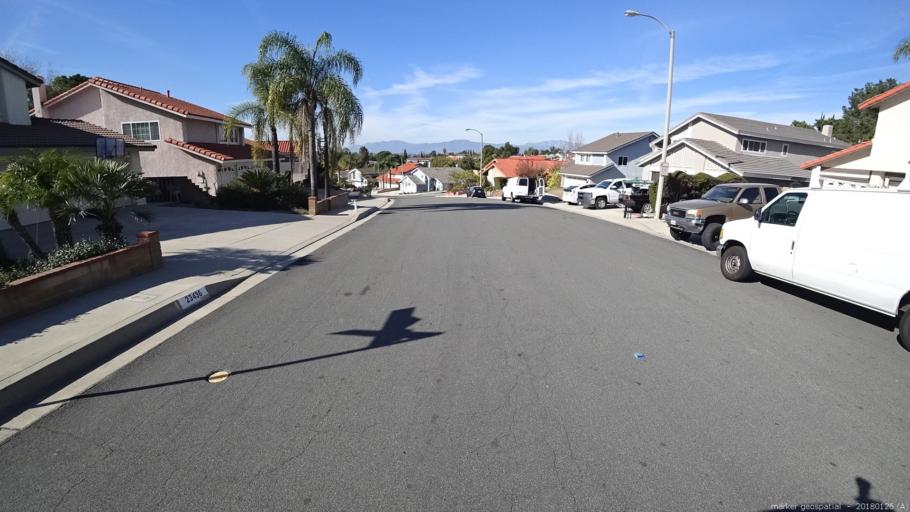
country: US
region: California
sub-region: Los Angeles County
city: Diamond Bar
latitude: 33.9947
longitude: -117.8064
